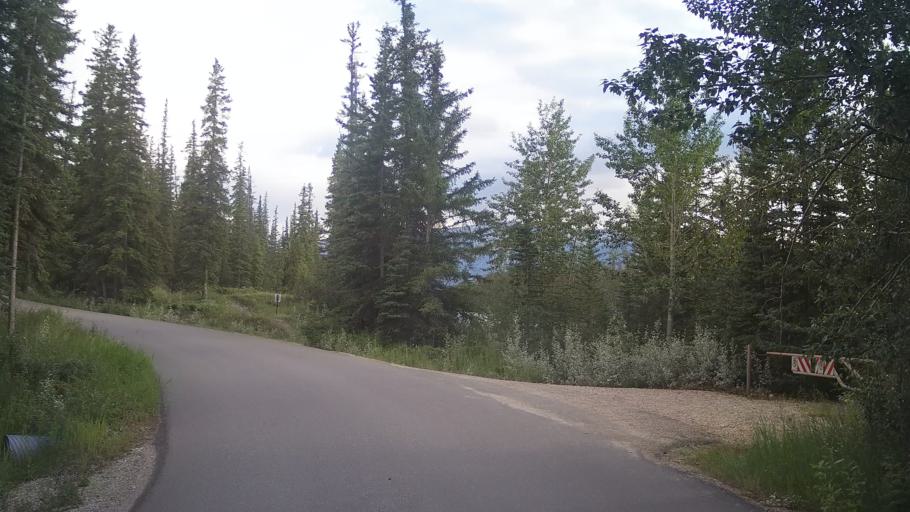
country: CA
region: Alberta
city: Jasper Park Lodge
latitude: 52.9325
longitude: -118.0331
